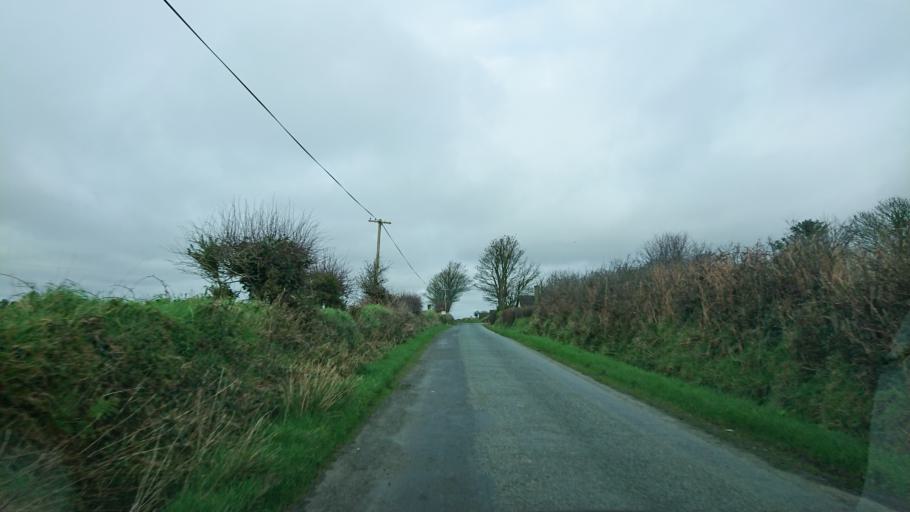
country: IE
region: Munster
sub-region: Waterford
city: Portlaw
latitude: 52.1754
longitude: -7.3041
